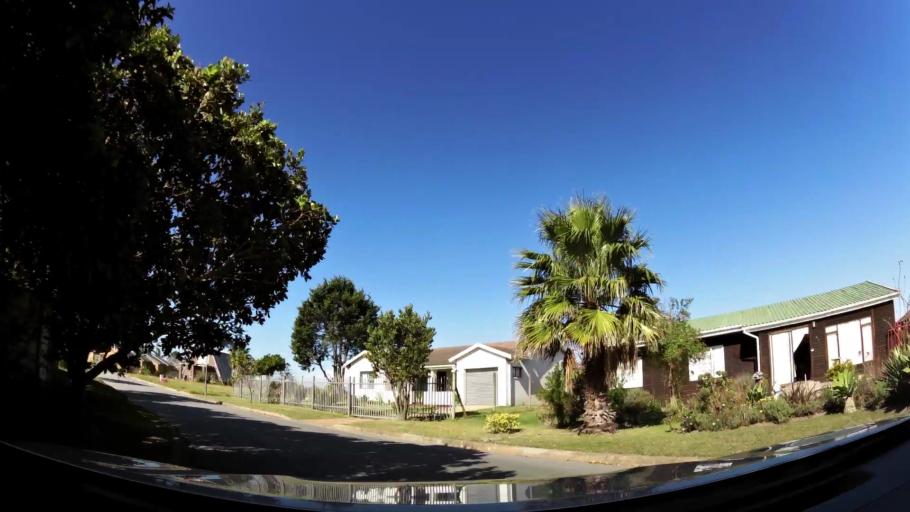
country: ZA
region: Western Cape
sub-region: Eden District Municipality
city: George
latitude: -33.9857
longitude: 22.4382
